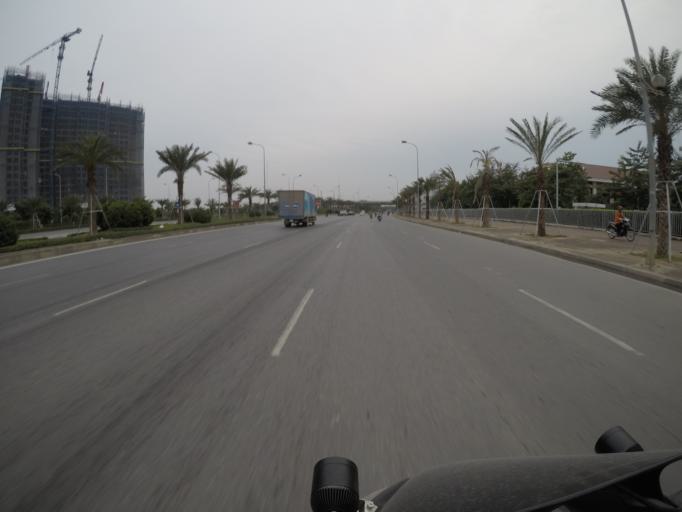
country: VN
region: Ha Noi
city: Thanh Xuan
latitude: 21.0025
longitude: 105.7843
